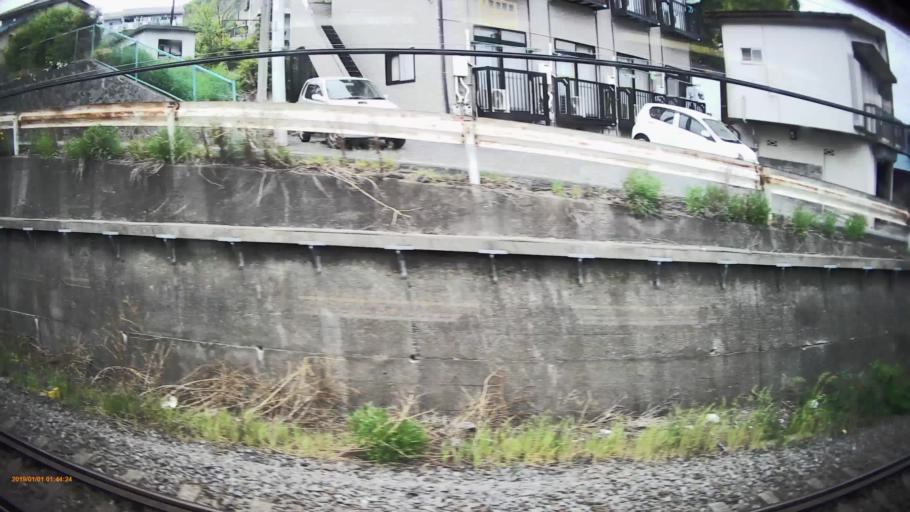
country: JP
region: Yamanashi
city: Kofu-shi
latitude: 35.6624
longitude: 138.5790
